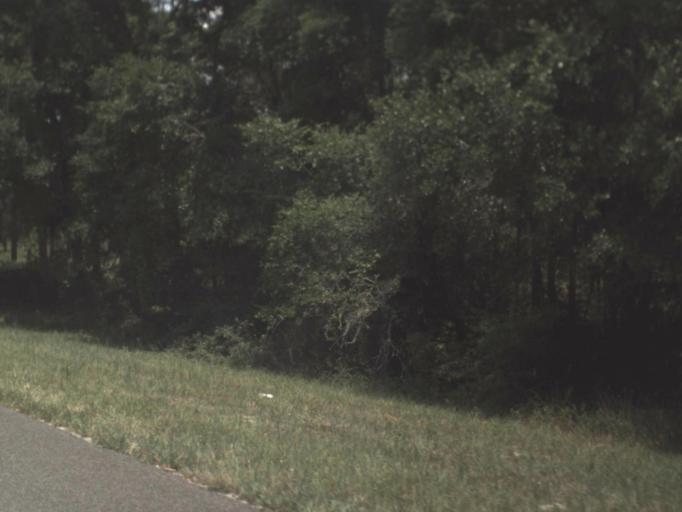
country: US
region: Florida
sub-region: Putnam County
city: Crescent City
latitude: 29.4215
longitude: -81.7372
